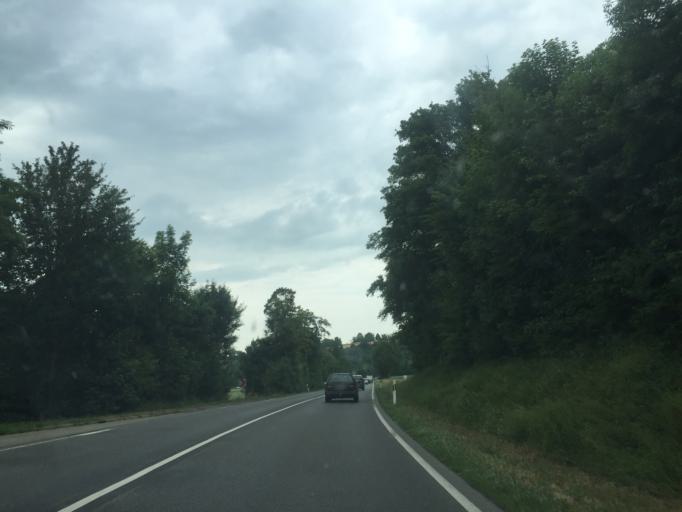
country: DE
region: Baden-Wuerttemberg
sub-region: Karlsruhe Region
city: Sinsheim
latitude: 49.2601
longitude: 8.8502
